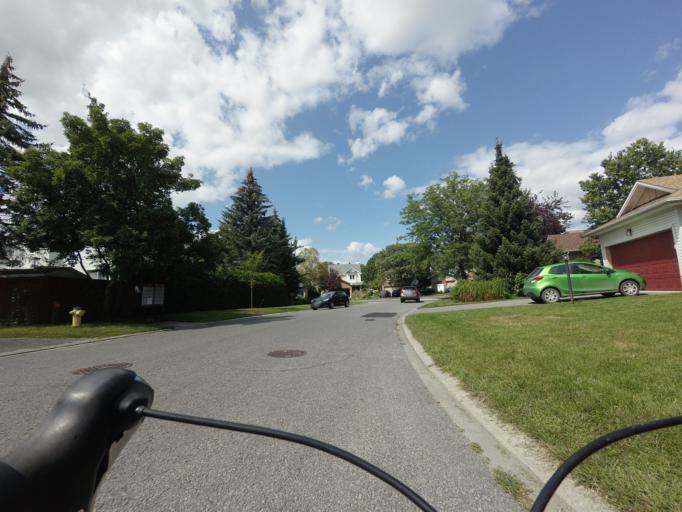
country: CA
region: Ontario
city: Bells Corners
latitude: 45.3013
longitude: -75.8575
